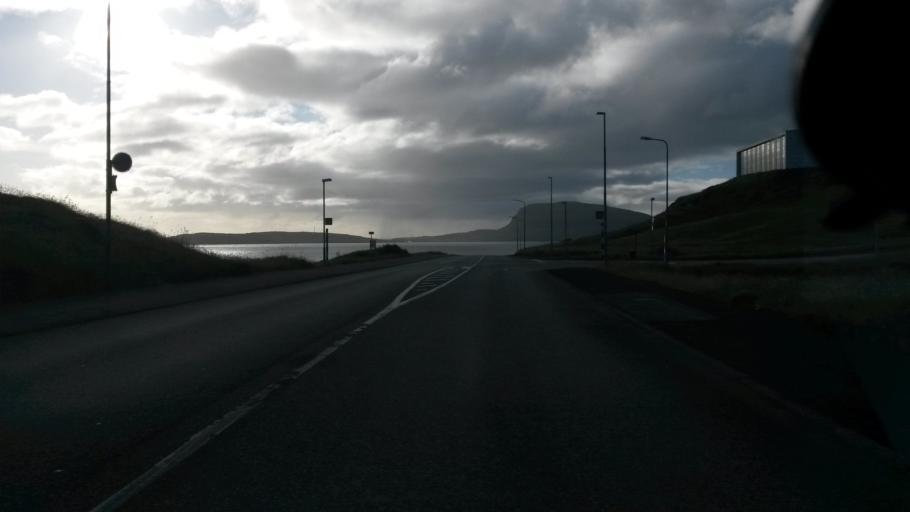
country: FO
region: Streymoy
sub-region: Torshavn
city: Torshavn
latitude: 62.0240
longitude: -6.7636
